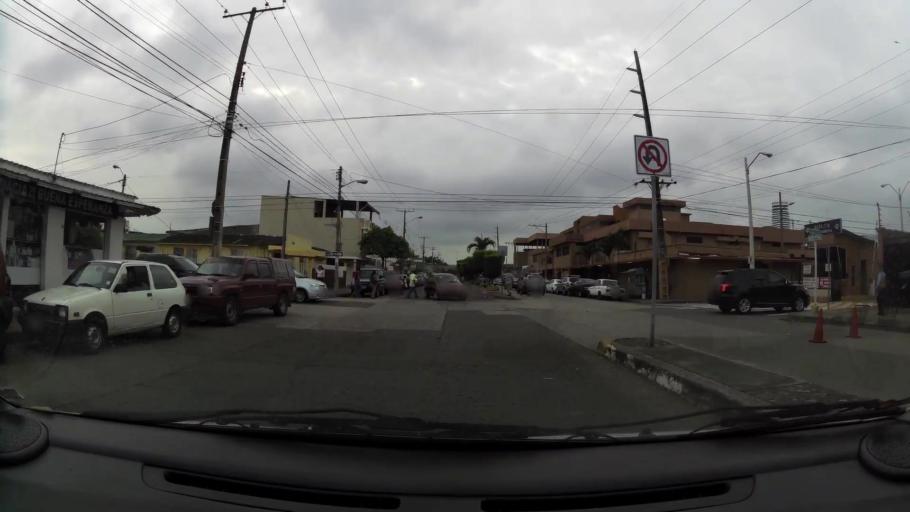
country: EC
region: Guayas
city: Eloy Alfaro
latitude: -2.1737
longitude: -79.8818
